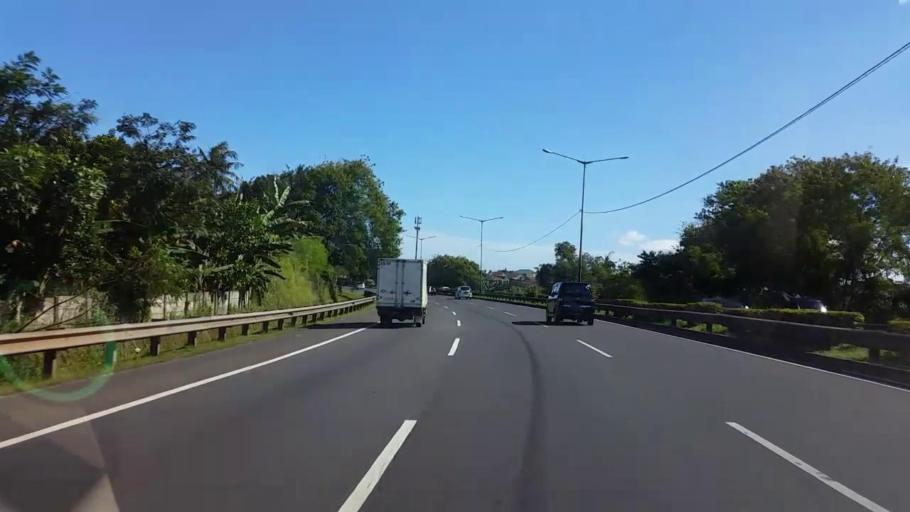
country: ID
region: Banten
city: South Tangerang
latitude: -6.2613
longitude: 106.7600
